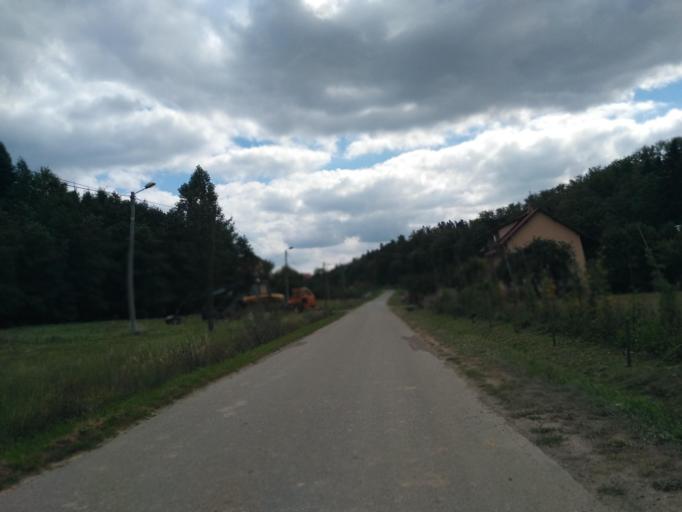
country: PL
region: Subcarpathian Voivodeship
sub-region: Powiat rzeszowski
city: Dynow
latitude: 49.7705
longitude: 22.2612
